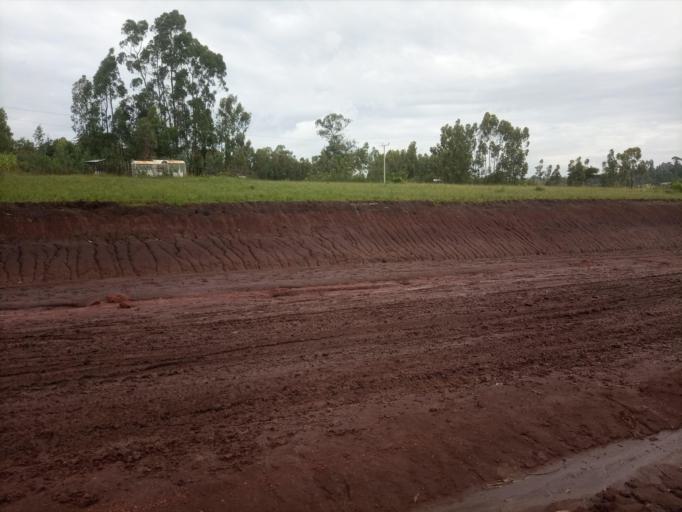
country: ET
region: Southern Nations, Nationalities, and People's Region
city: K'olito
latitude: 7.3021
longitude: 37.9318
